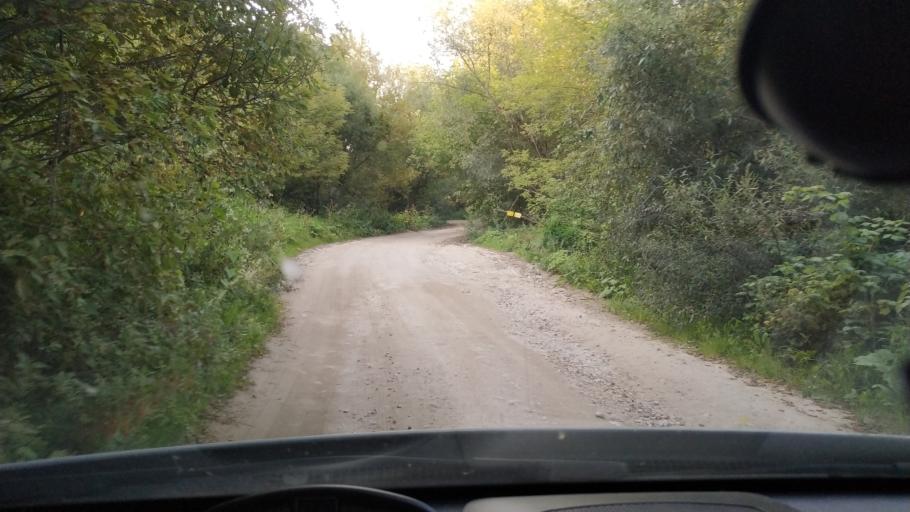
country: RU
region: Rjazan
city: Rybnoye
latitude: 54.8679
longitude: 39.6528
